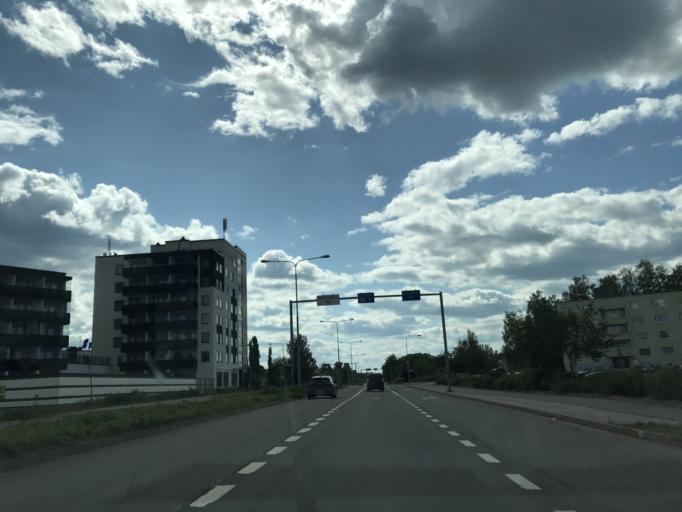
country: FI
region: Uusimaa
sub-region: Helsinki
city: Maentsaelae
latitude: 60.6363
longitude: 25.3172
